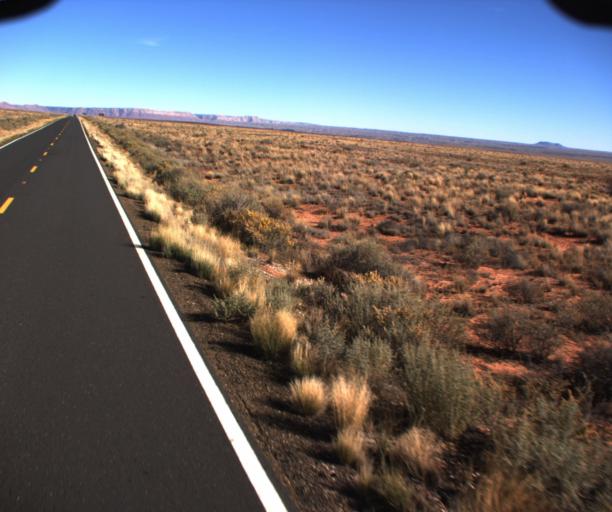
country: US
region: Arizona
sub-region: Coconino County
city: Page
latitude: 36.6975
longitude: -111.9152
